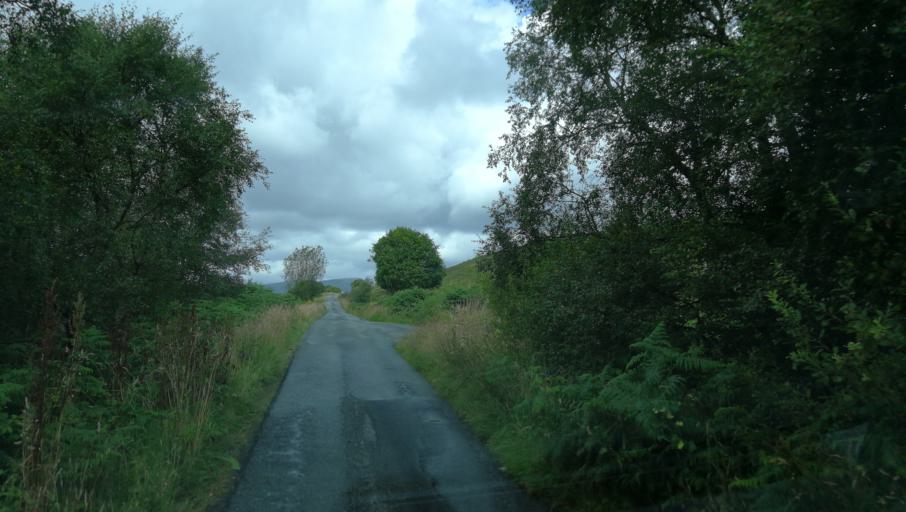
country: GB
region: Scotland
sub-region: Highland
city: Portree
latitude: 57.3824
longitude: -6.1945
